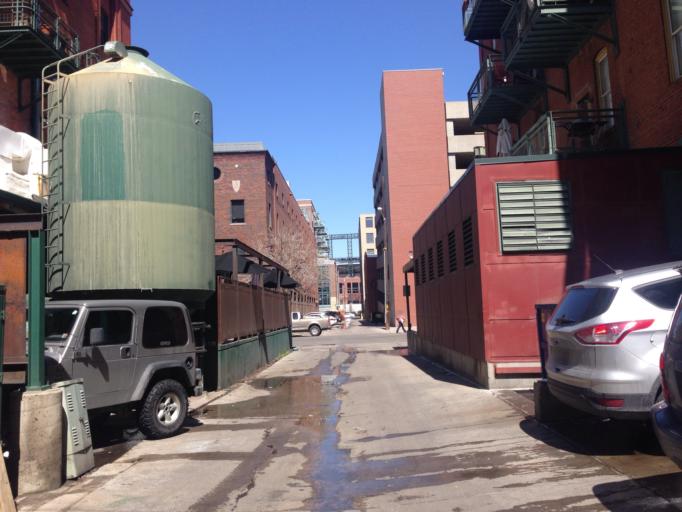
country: US
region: Colorado
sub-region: Denver County
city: Denver
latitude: 39.7532
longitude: -104.9985
